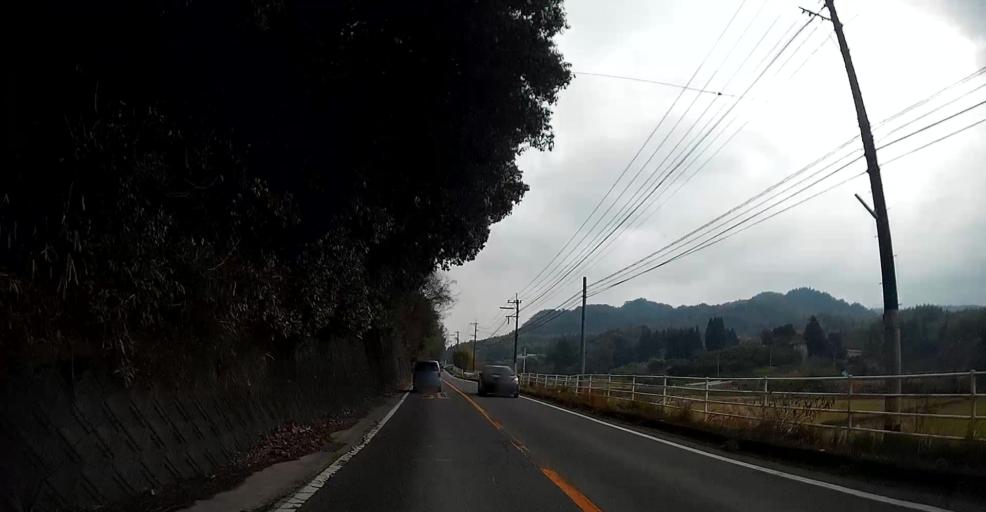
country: JP
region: Kumamoto
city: Matsubase
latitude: 32.6477
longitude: 130.7226
